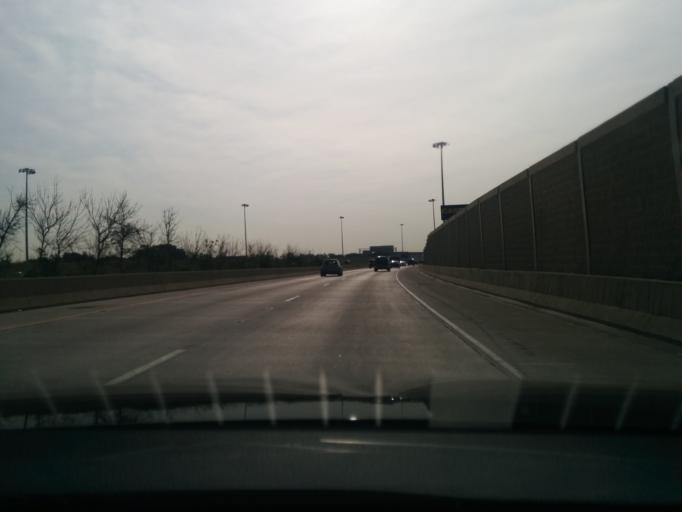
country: US
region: Illinois
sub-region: Cook County
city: Hillside
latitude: 41.8733
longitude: -87.9019
